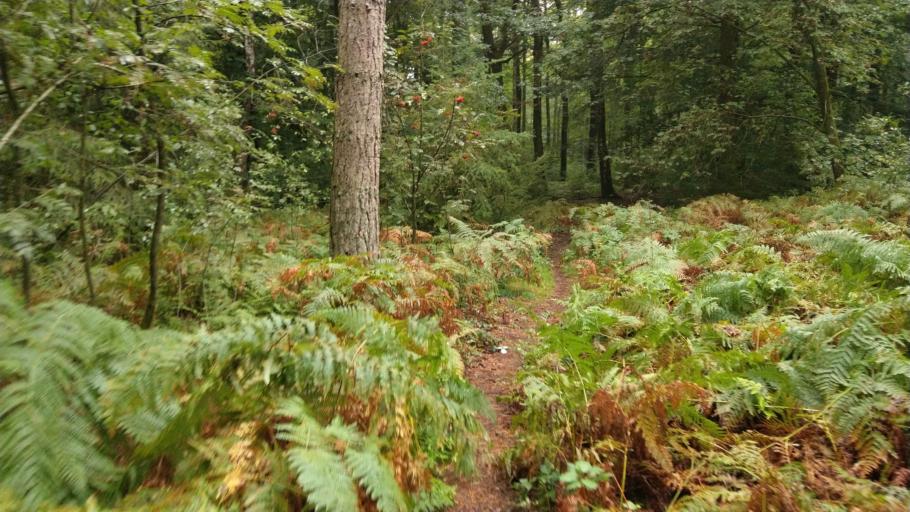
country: NL
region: Limburg
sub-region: Gemeente Vaals
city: Vaals
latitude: 50.7474
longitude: 6.0339
